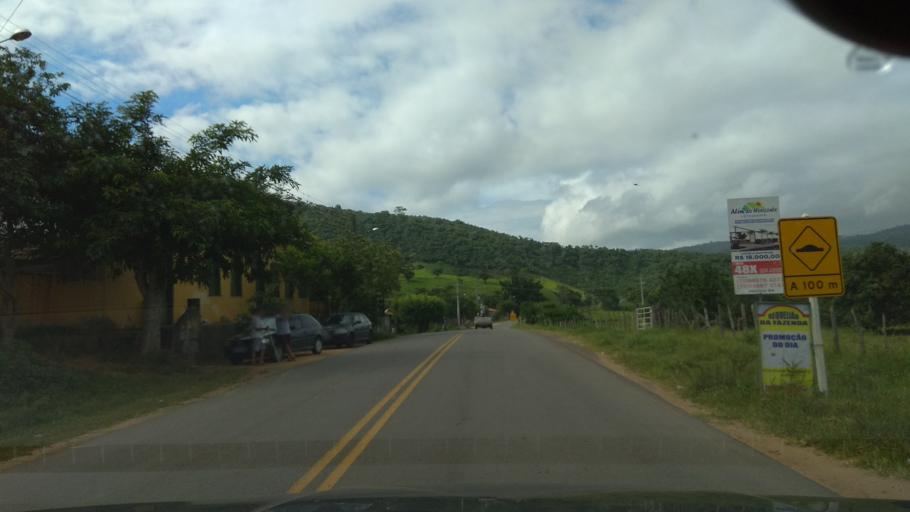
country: BR
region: Bahia
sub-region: Ubaira
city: Ubaira
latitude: -13.2524
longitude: -39.7140
